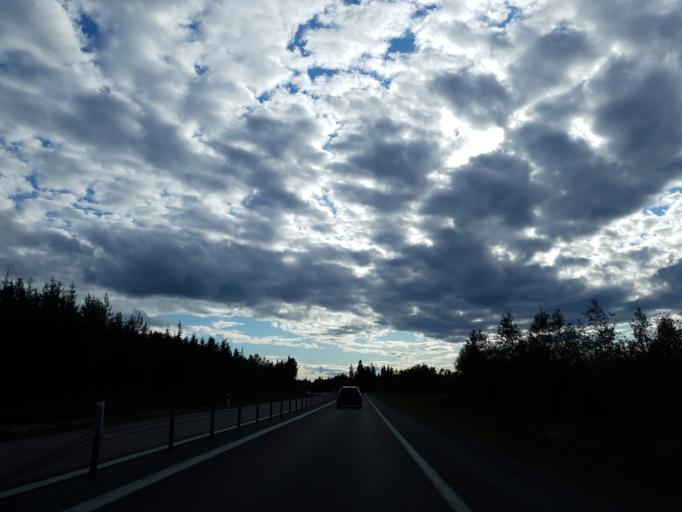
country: SE
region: Vaesternorrland
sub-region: Haernoesands Kommun
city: Haernoesand
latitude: 62.6083
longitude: 17.8283
